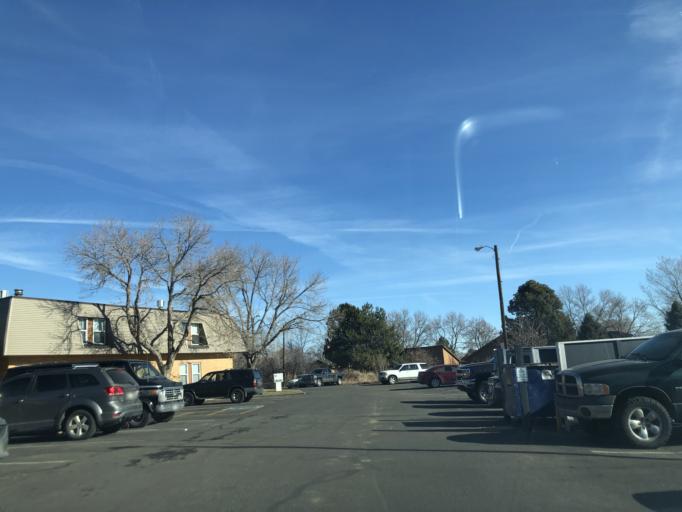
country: US
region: Colorado
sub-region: Adams County
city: Aurora
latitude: 39.7144
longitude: -104.8175
